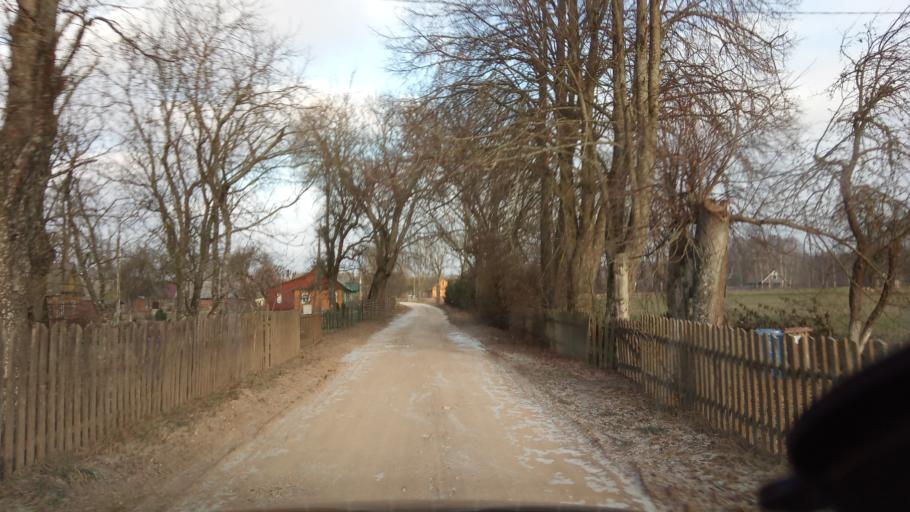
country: LT
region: Alytaus apskritis
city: Varena
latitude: 54.1272
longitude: 24.6466
